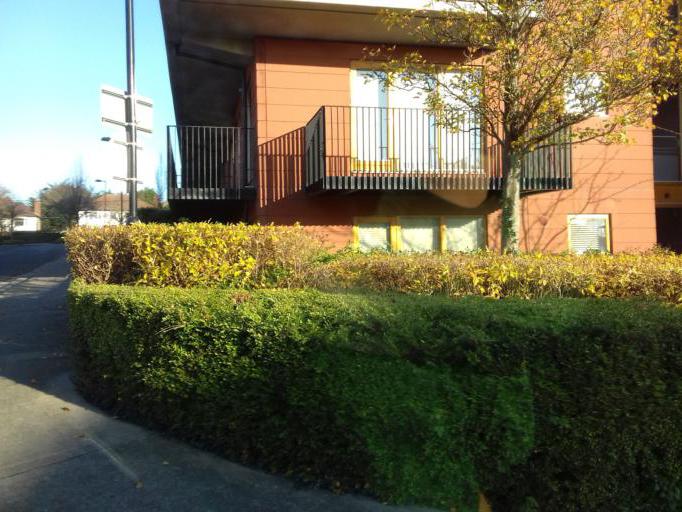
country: IE
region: Leinster
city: Glasnevin
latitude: 53.3771
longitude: -6.2780
